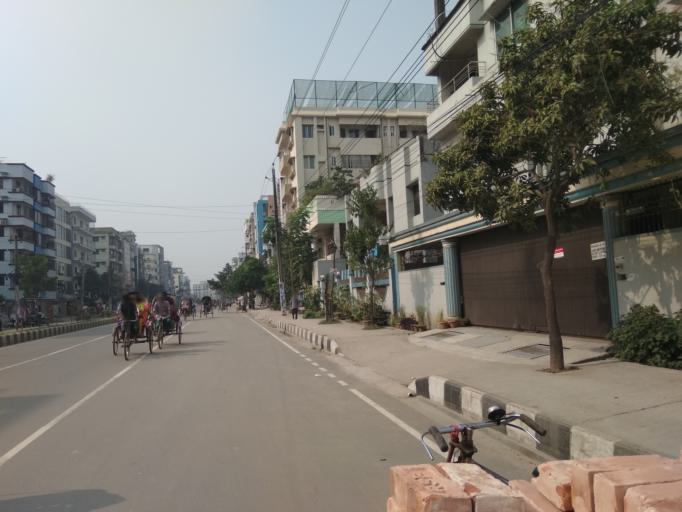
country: BD
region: Dhaka
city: Tungi
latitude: 23.8695
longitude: 90.3887
